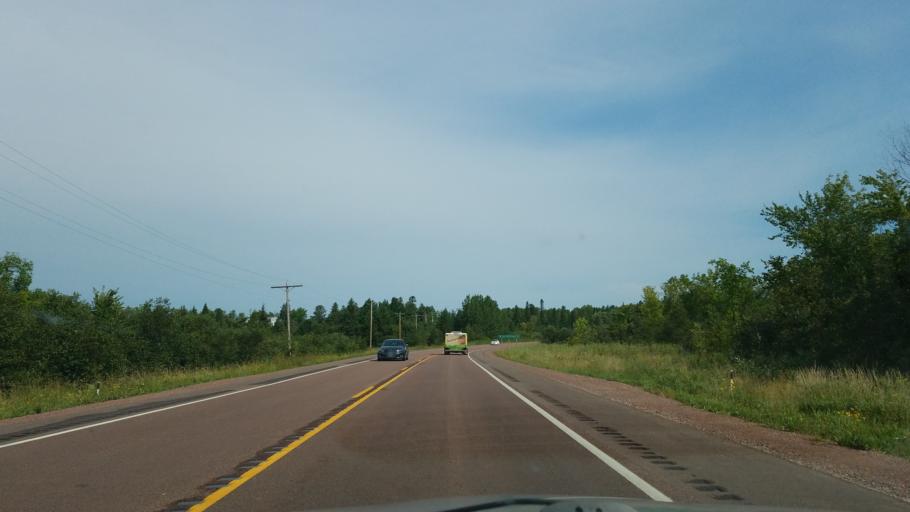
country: US
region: Wisconsin
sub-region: Ashland County
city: Ashland
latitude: 46.5989
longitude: -90.9551
